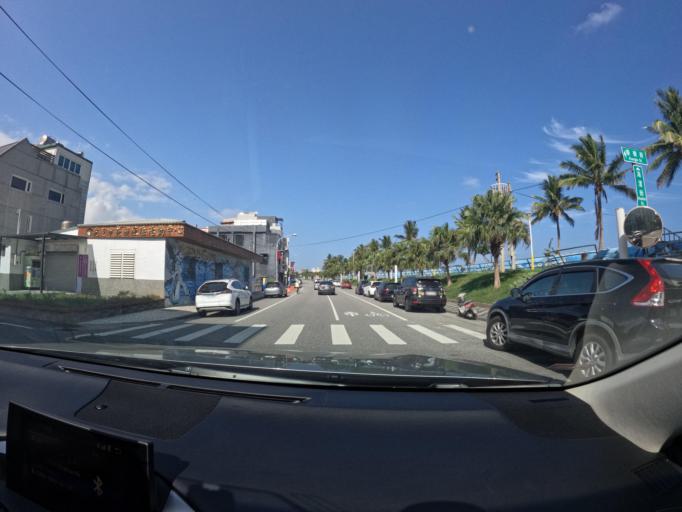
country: TW
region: Taiwan
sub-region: Hualien
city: Hualian
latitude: 23.9738
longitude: 121.6153
